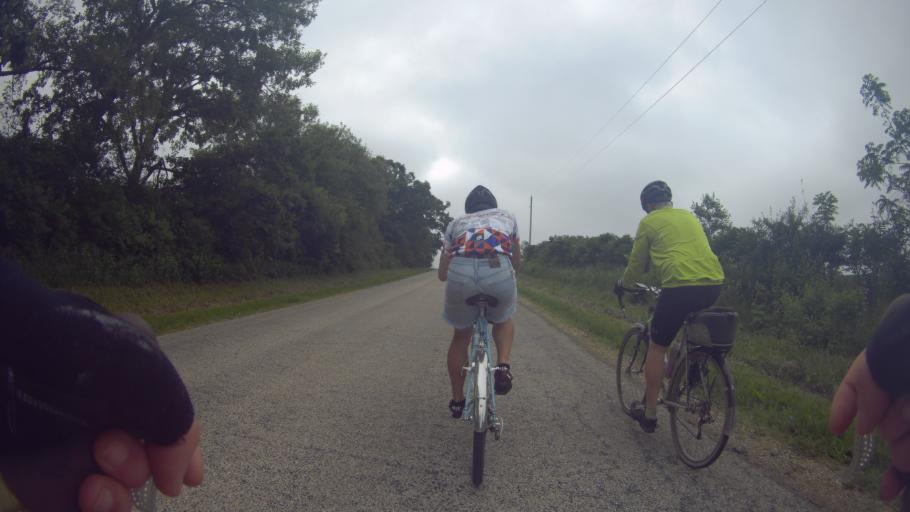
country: US
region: Wisconsin
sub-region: Green County
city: Brooklyn
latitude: 42.8427
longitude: -89.4144
